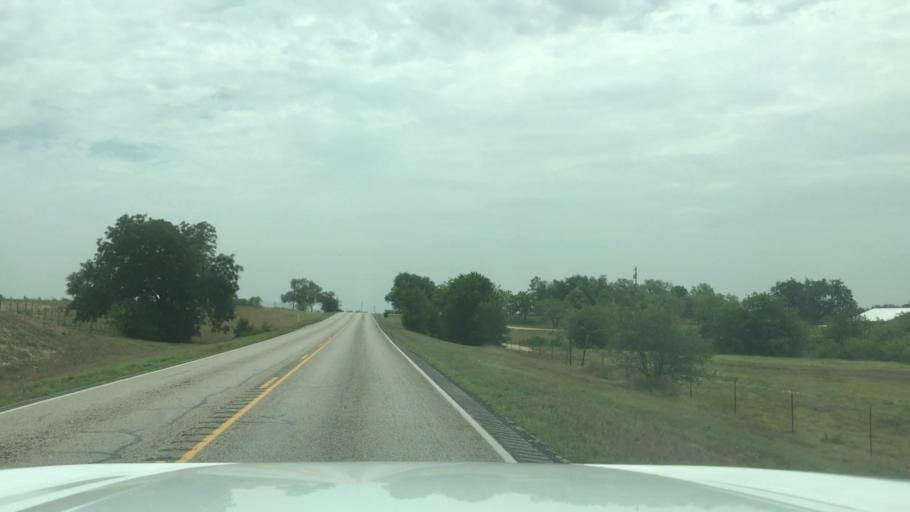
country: US
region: Texas
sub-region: Hamilton County
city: Hico
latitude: 32.0455
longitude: -98.1439
